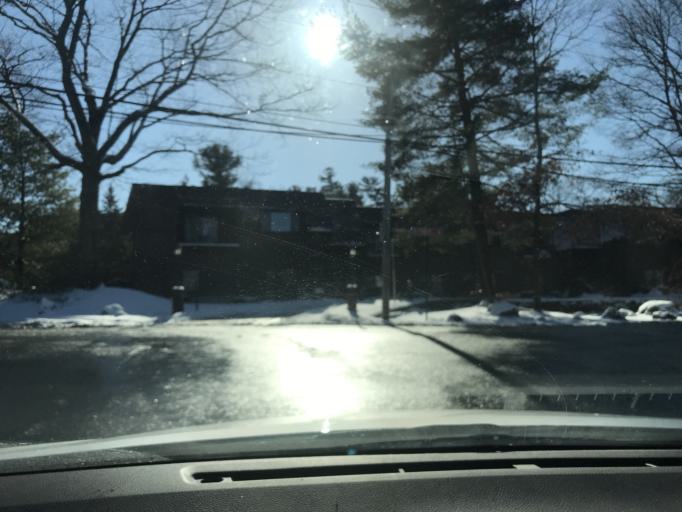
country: US
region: Massachusetts
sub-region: Essex County
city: Saugus
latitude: 42.4787
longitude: -71.0257
